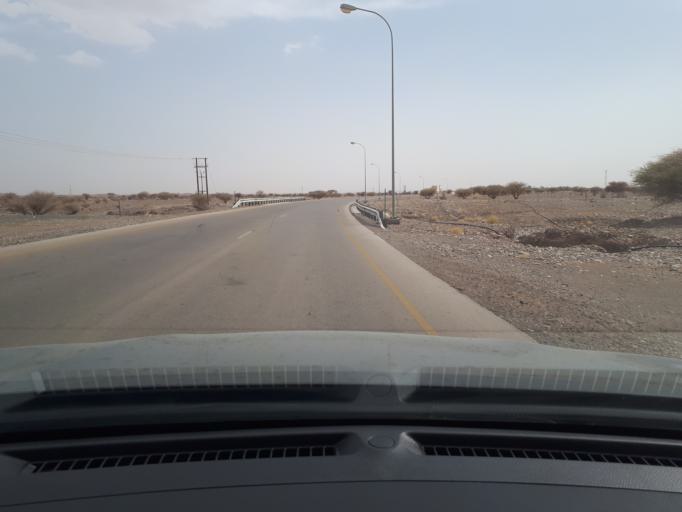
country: OM
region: Ash Sharqiyah
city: Badiyah
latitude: 22.5055
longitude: 58.9471
